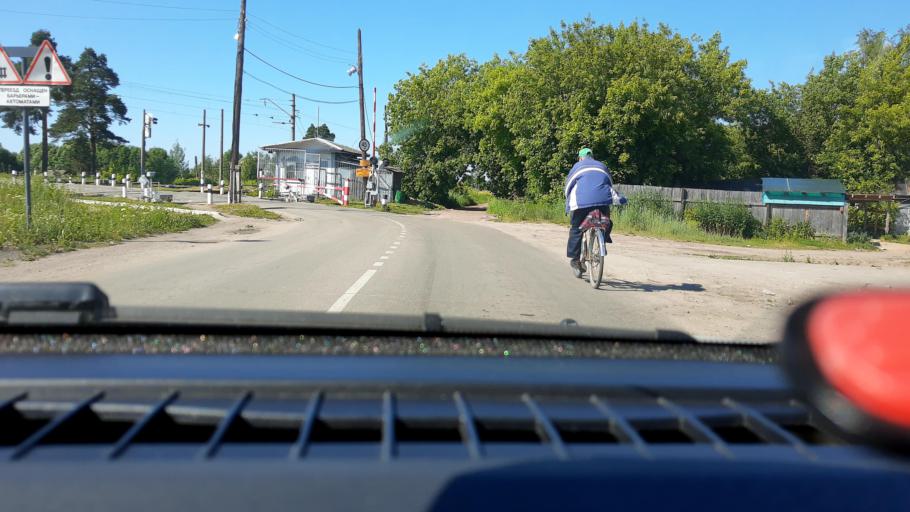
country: RU
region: Nizjnij Novgorod
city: Gidrotorf
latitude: 56.5228
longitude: 43.5455
